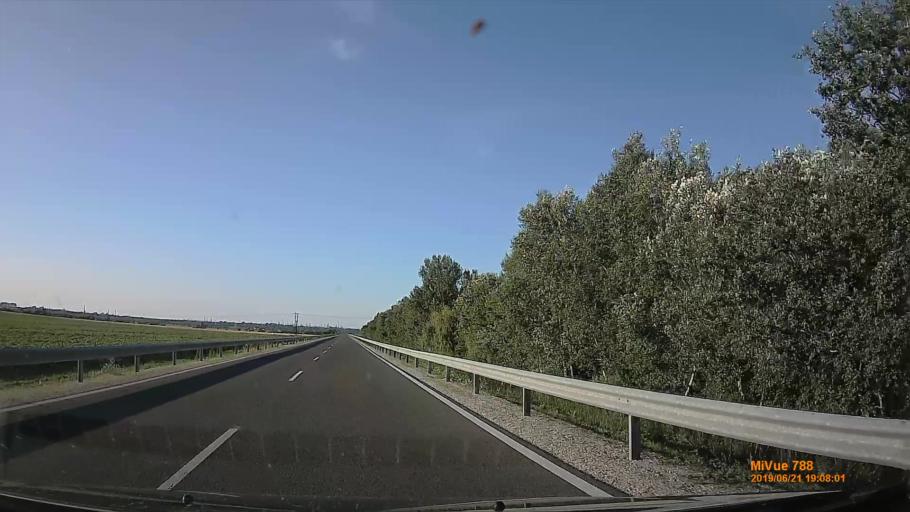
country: HU
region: Fejer
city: Ercsi
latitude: 47.2104
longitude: 18.8841
